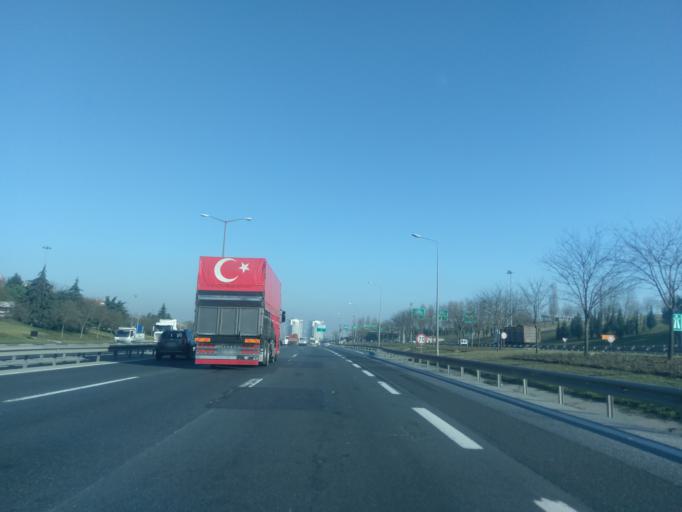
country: TR
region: Istanbul
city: Esenyurt
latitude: 41.0535
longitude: 28.6716
